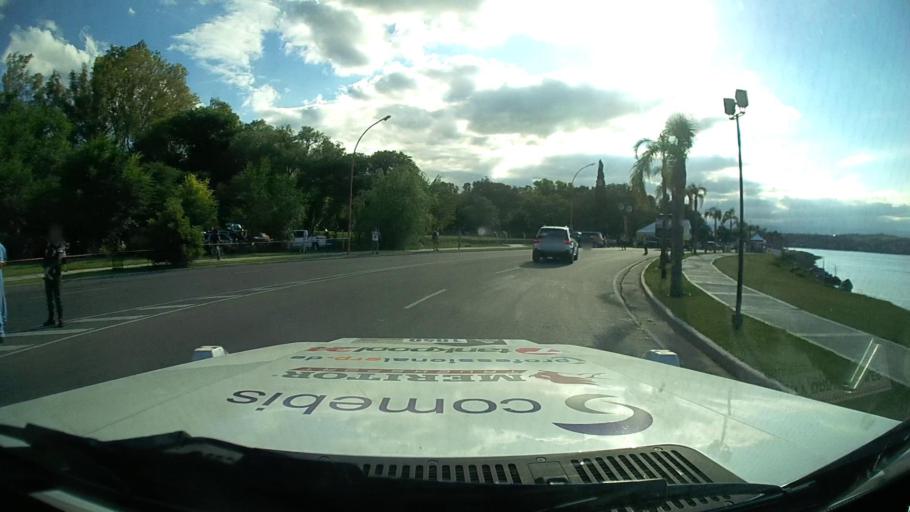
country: AR
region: Cordoba
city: Villa Carlos Paz
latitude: -31.3954
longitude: -64.4724
